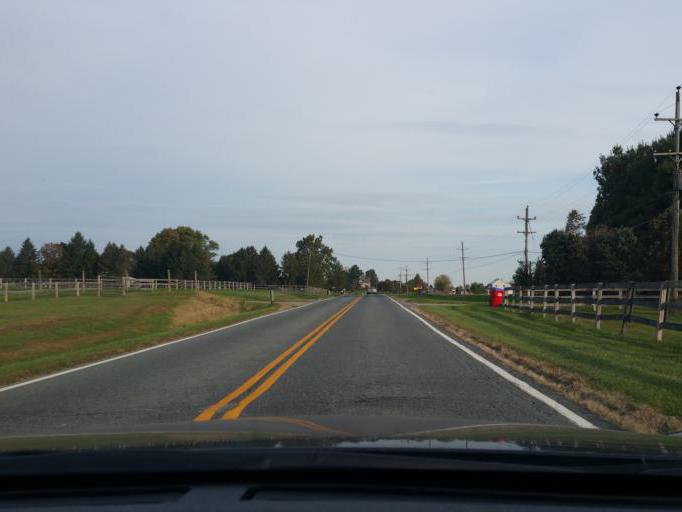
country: US
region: Maryland
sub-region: Cecil County
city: Rising Sun
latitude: 39.7072
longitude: -76.0259
